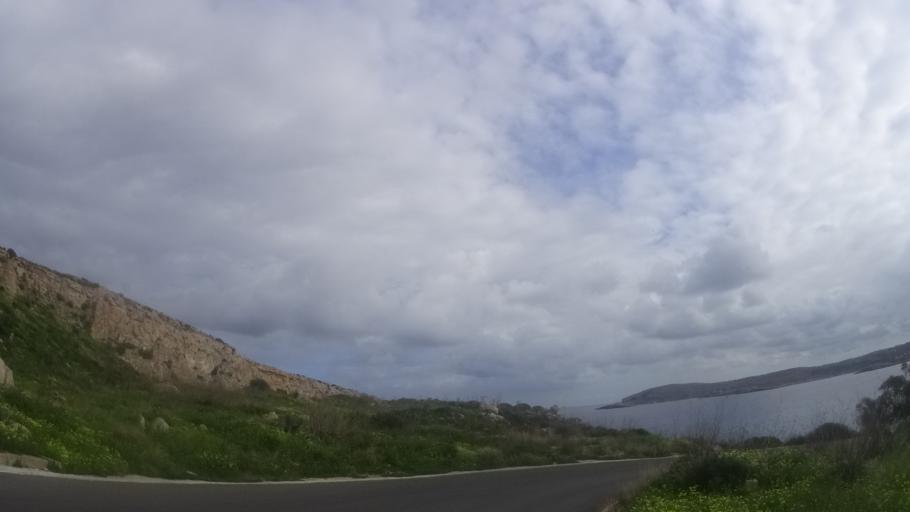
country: MT
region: Il-Qala
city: Qala
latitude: 36.0288
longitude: 14.3226
